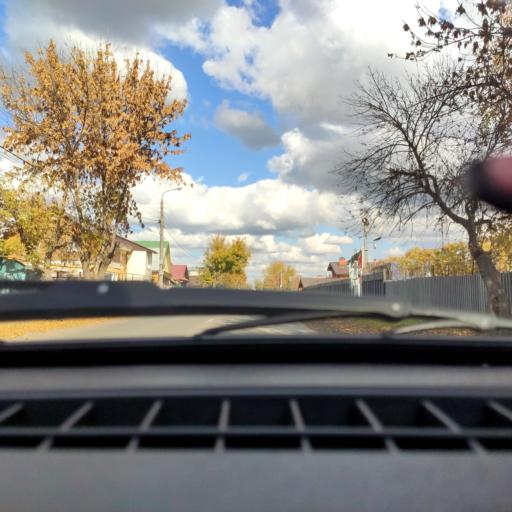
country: RU
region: Bashkortostan
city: Ufa
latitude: 54.7263
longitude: 55.9106
